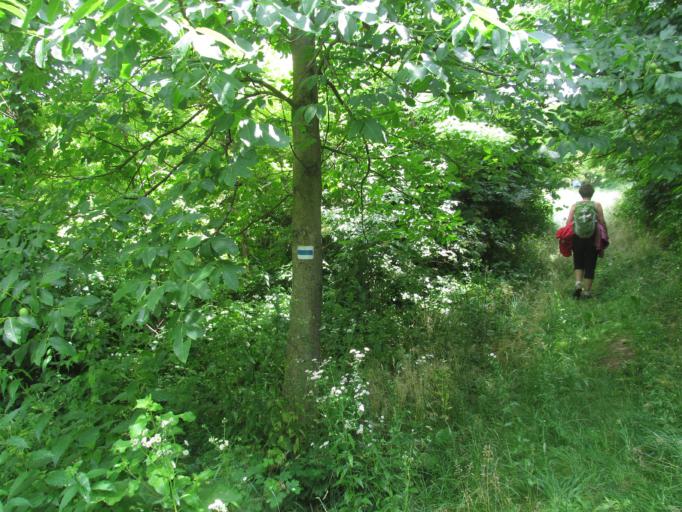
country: HU
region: Veszprem
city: Badacsonytomaj
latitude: 46.8781
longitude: 17.5189
